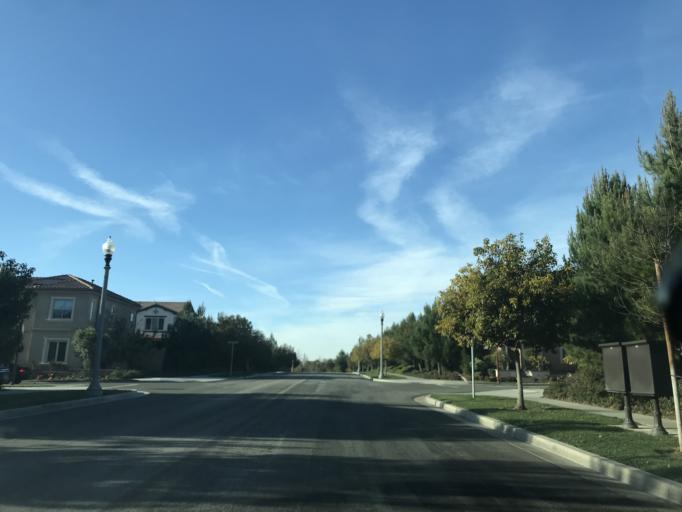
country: US
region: California
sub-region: Orange County
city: North Tustin
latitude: 33.7117
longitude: -117.7416
